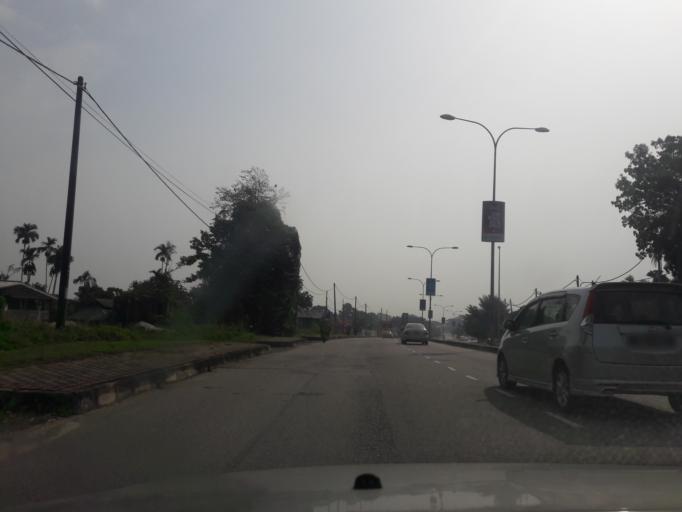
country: MY
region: Kedah
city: Kulim
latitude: 5.3603
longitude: 100.5454
